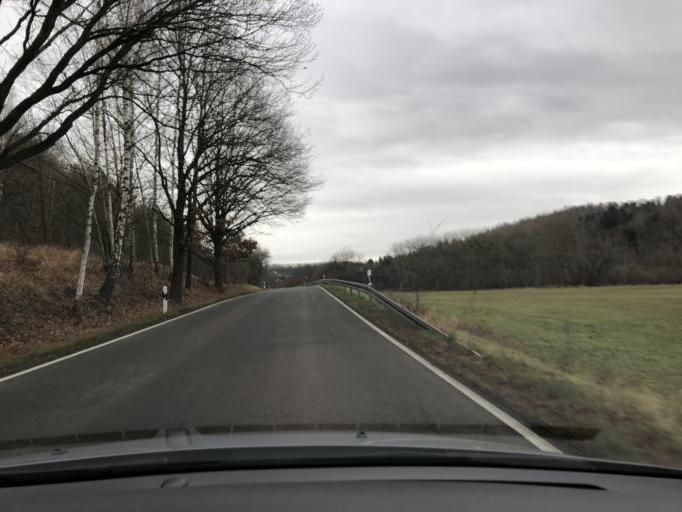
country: DE
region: Saxony
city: Rosswein
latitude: 51.0682
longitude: 13.2198
